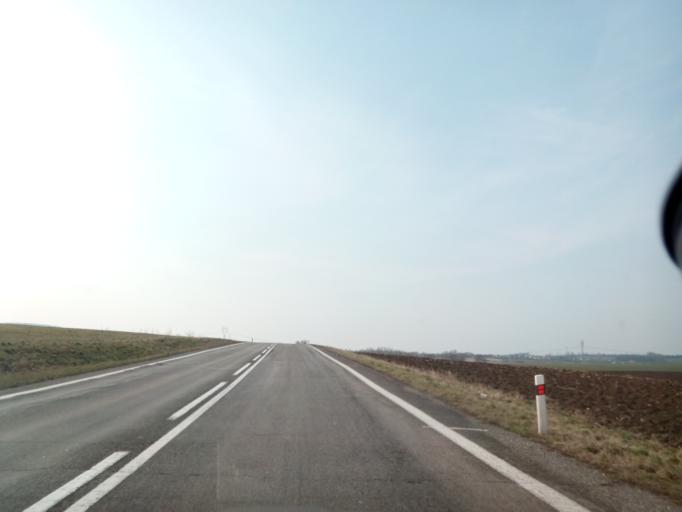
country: SK
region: Kosicky
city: Trebisov
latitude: 48.5360
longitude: 21.6793
